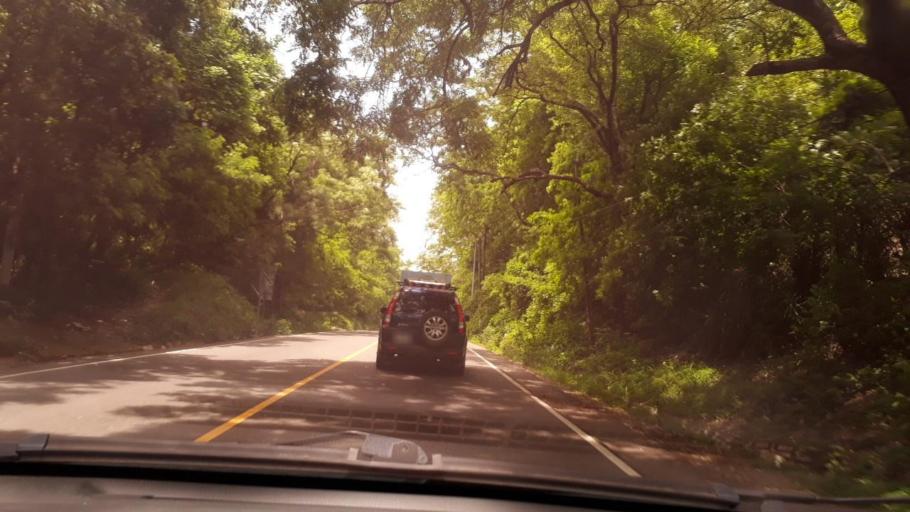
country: GT
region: Chiquimula
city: San Jacinto
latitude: 14.6552
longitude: -89.4902
